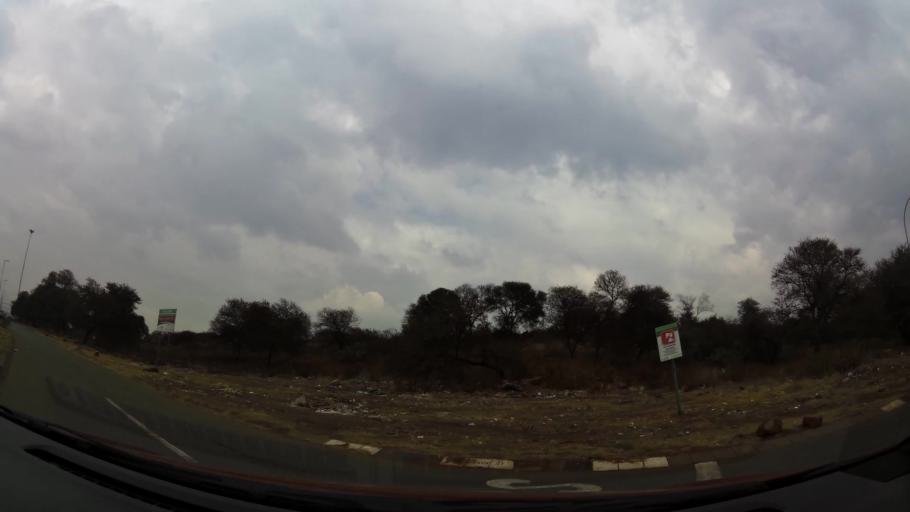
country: ZA
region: Gauteng
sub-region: City of Johannesburg Metropolitan Municipality
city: Soweto
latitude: -26.2614
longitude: 27.8311
